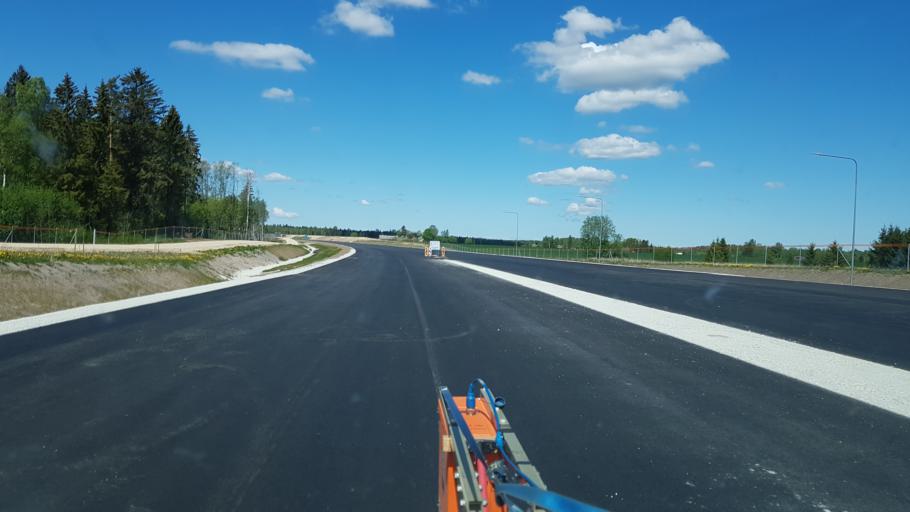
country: EE
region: Harju
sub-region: Anija vald
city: Kehra
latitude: 59.1075
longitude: 25.3127
